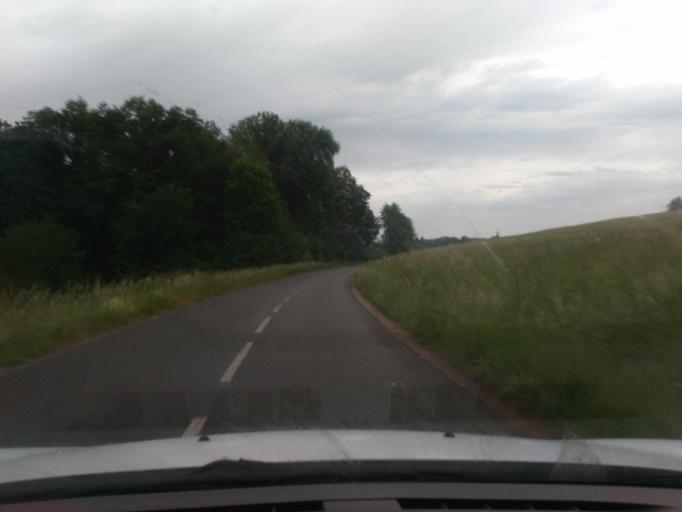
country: FR
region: Lorraine
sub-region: Departement des Vosges
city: Jeanmenil
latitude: 48.2874
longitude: 6.6970
